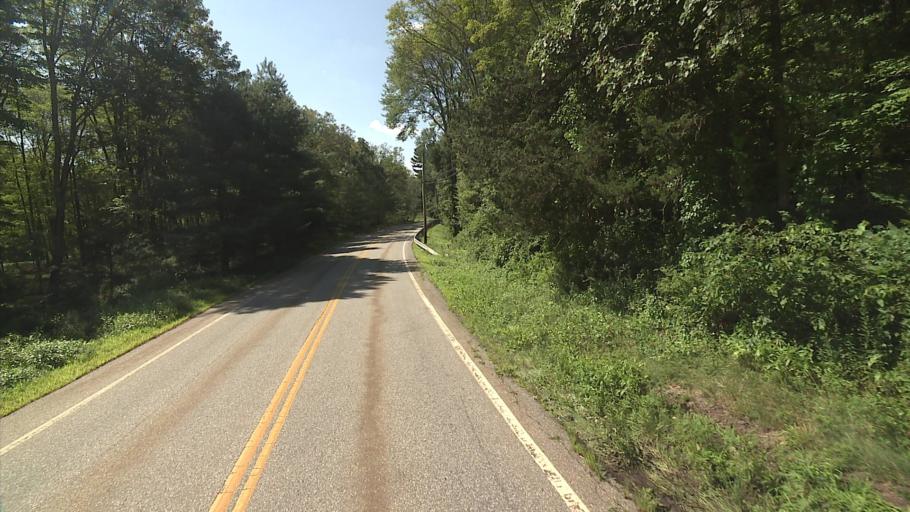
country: US
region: Connecticut
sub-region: Tolland County
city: Storrs
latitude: 41.8327
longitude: -72.1699
